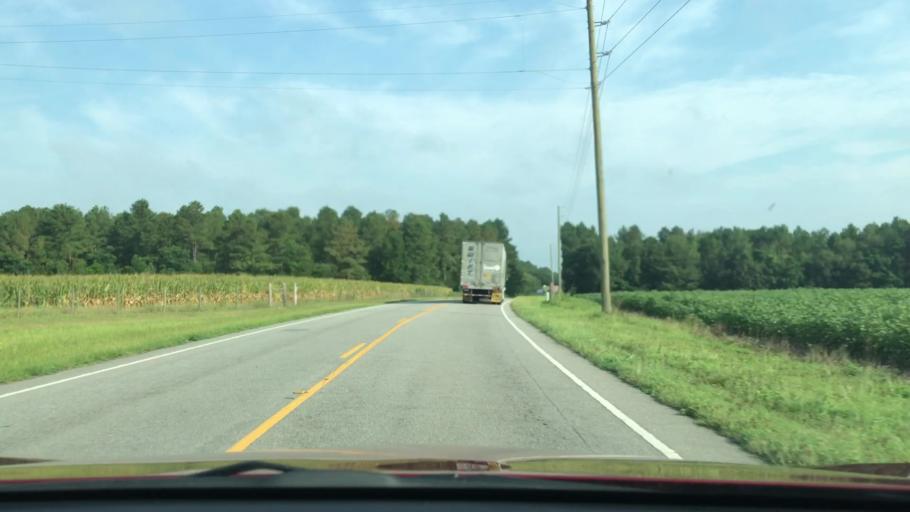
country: US
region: South Carolina
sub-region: Barnwell County
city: Blackville
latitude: 33.6004
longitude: -81.2623
